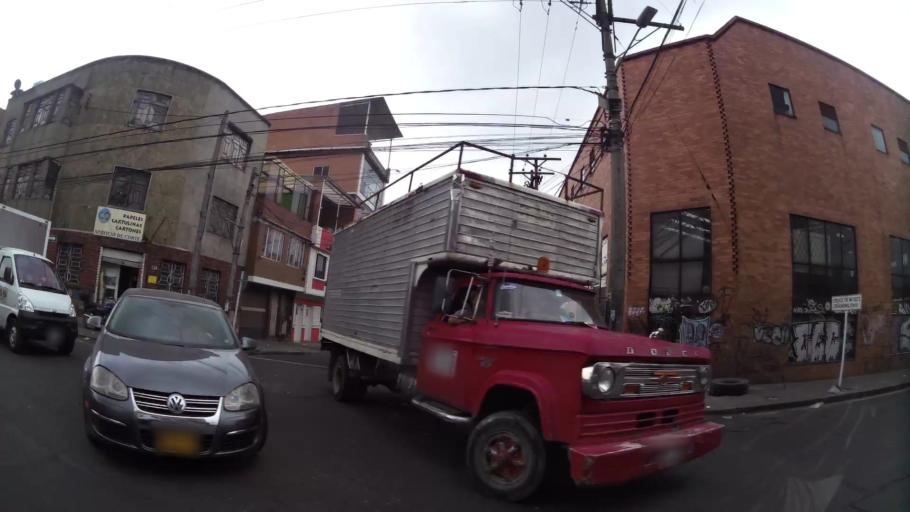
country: CO
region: Bogota D.C.
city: Bogota
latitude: 4.6024
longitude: -74.0935
